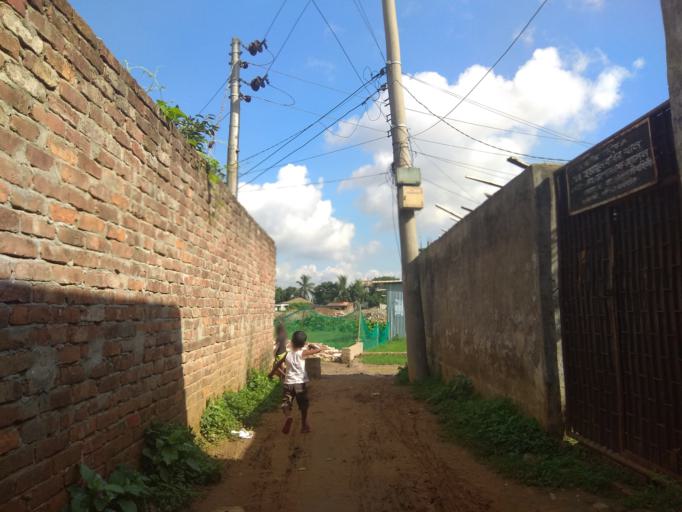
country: BD
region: Dhaka
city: Paltan
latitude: 23.8111
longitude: 90.3869
